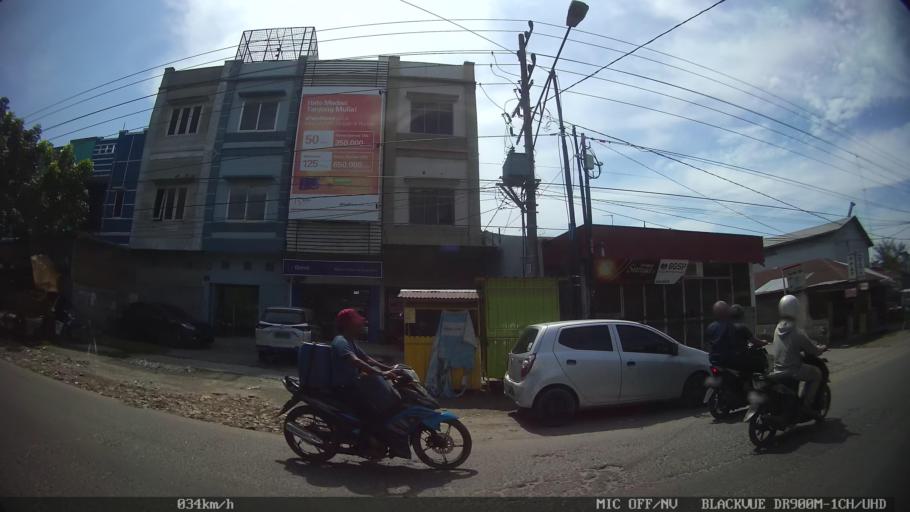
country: ID
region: North Sumatra
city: Labuhan Deli
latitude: 3.6782
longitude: 98.6560
